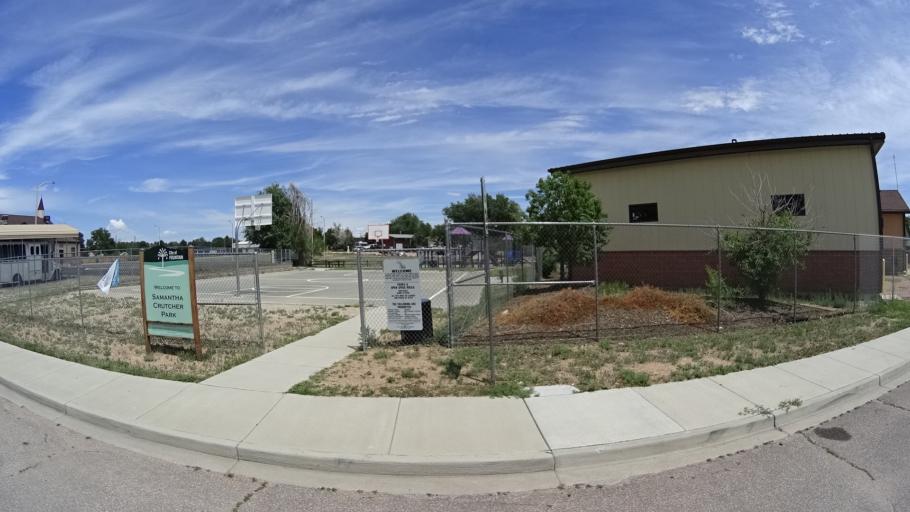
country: US
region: Colorado
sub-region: El Paso County
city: Security-Widefield
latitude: 38.7278
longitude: -104.7273
